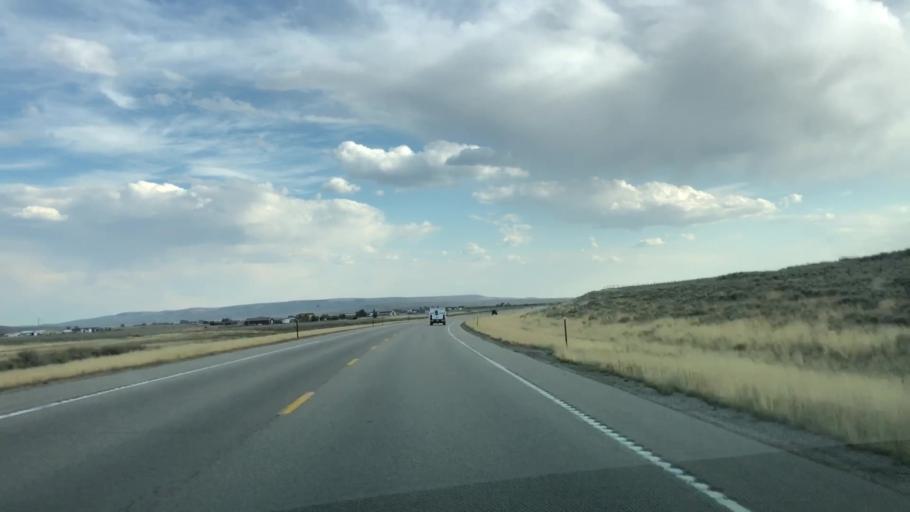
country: US
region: Wyoming
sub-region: Sublette County
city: Pinedale
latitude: 42.9957
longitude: -110.0951
